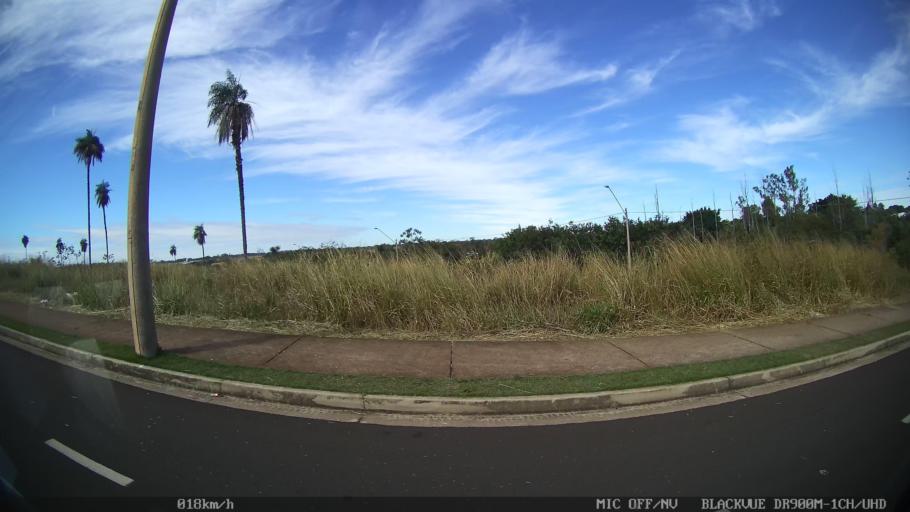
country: BR
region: Sao Paulo
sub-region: Sao Jose Do Rio Preto
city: Sao Jose do Rio Preto
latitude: -20.8590
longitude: -49.3803
